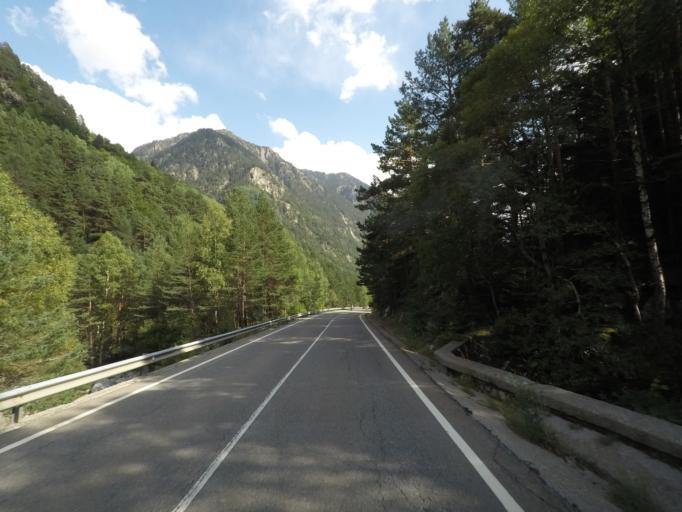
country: ES
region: Aragon
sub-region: Provincia de Huesca
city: Bielsa
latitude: 42.6919
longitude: 0.2052
